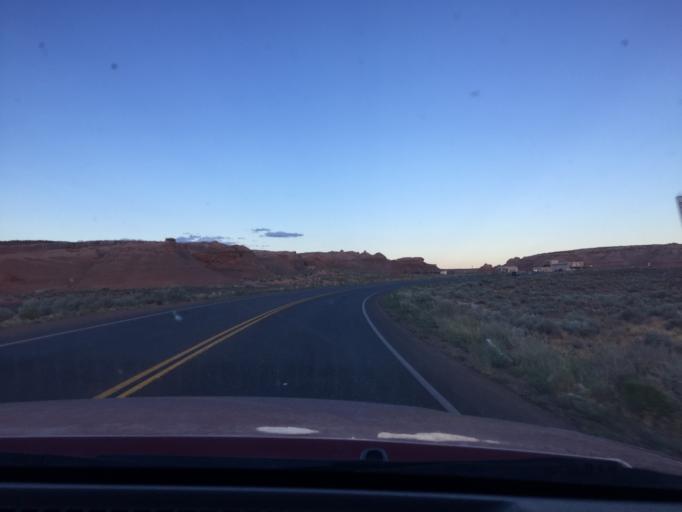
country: US
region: Arizona
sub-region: Coconino County
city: Page
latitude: 36.8980
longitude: -111.4489
